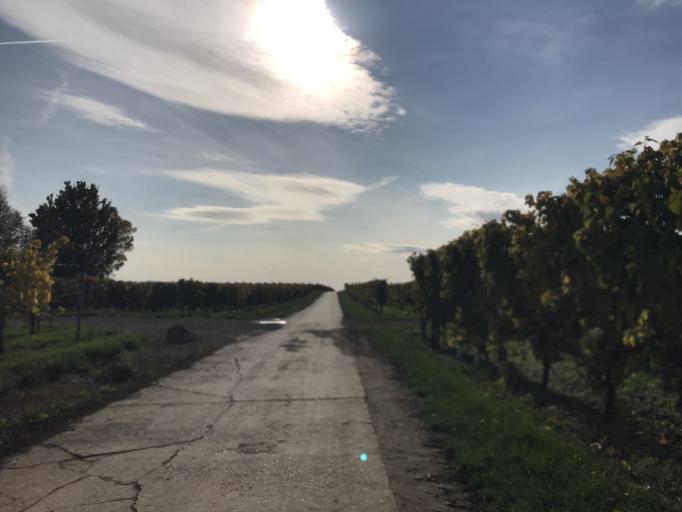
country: DE
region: Rheinland-Pfalz
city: Essenheim
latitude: 49.9247
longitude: 8.1495
